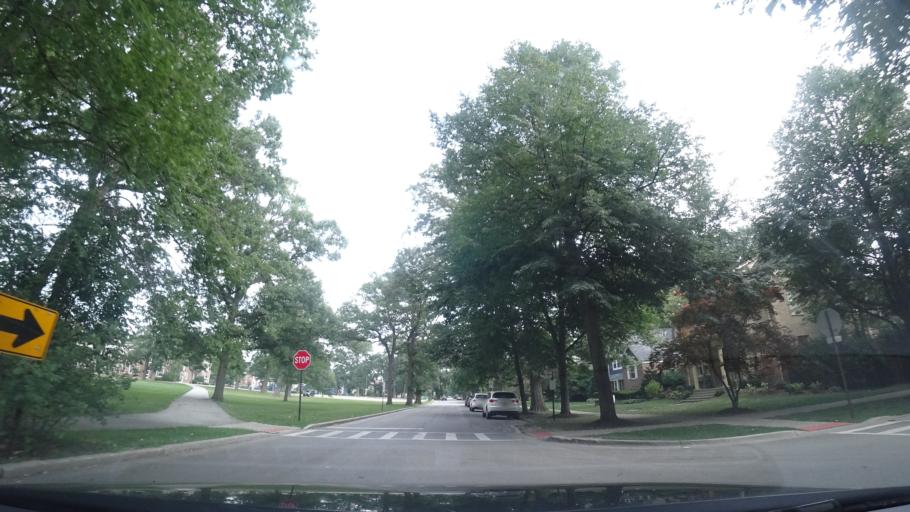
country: US
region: Illinois
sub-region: Cook County
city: Wilmette
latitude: 42.0591
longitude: -87.7109
